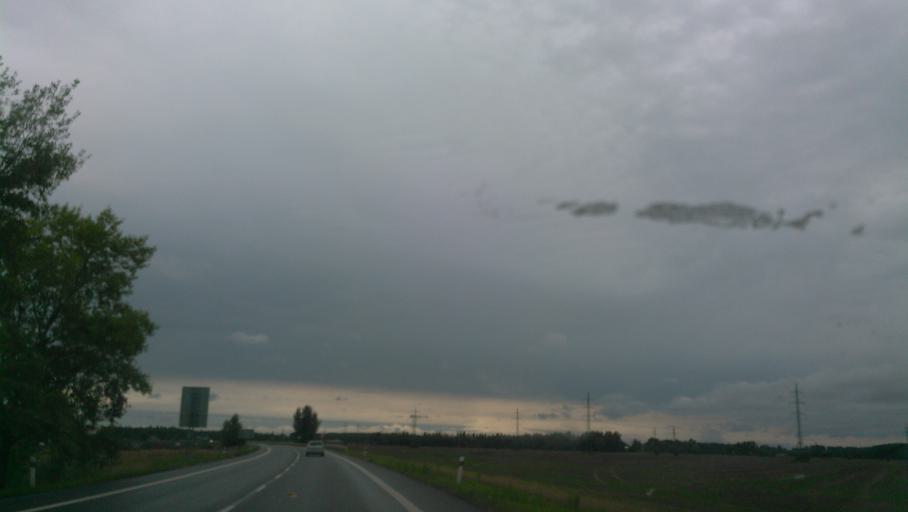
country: SK
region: Trnavsky
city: Dunajska Streda
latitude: 47.9897
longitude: 17.5834
